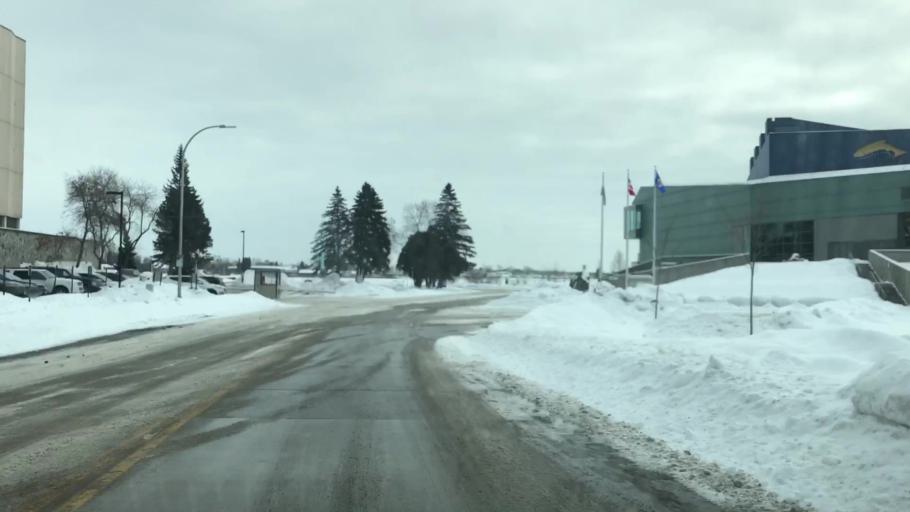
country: US
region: Minnesota
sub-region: Saint Louis County
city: Duluth
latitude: 46.7801
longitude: -92.1006
